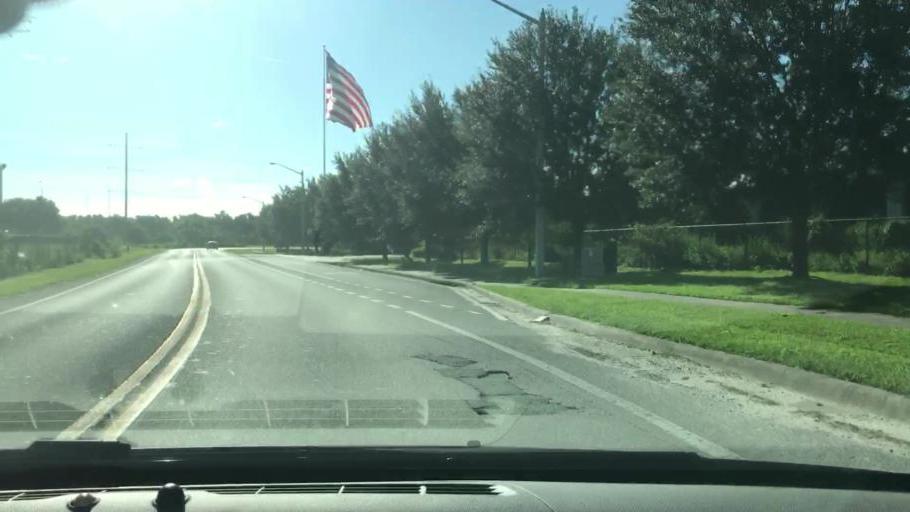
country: US
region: Florida
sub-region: Marion County
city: Ocala
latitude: 29.1849
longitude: -82.1875
